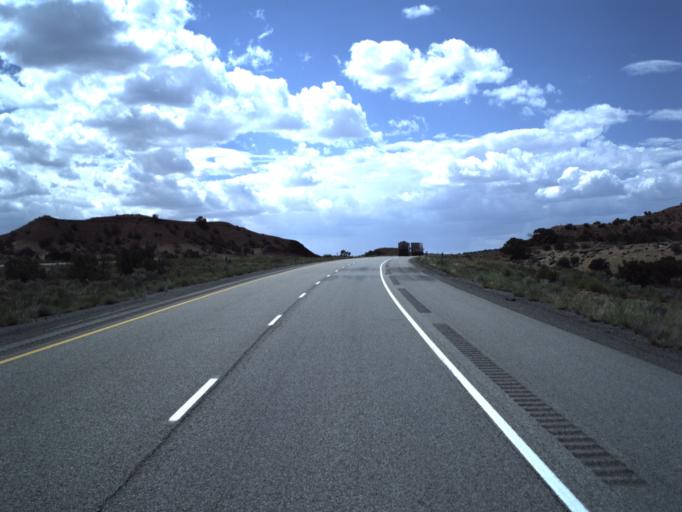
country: US
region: Utah
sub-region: Emery County
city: Castle Dale
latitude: 38.8676
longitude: -110.7063
